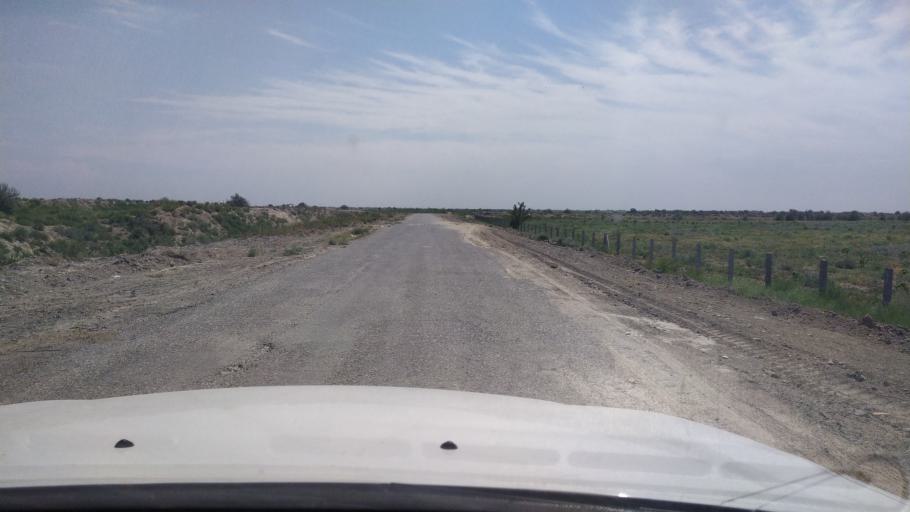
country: UZ
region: Namangan
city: Toshbuloq
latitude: 40.7895
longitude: 71.5610
